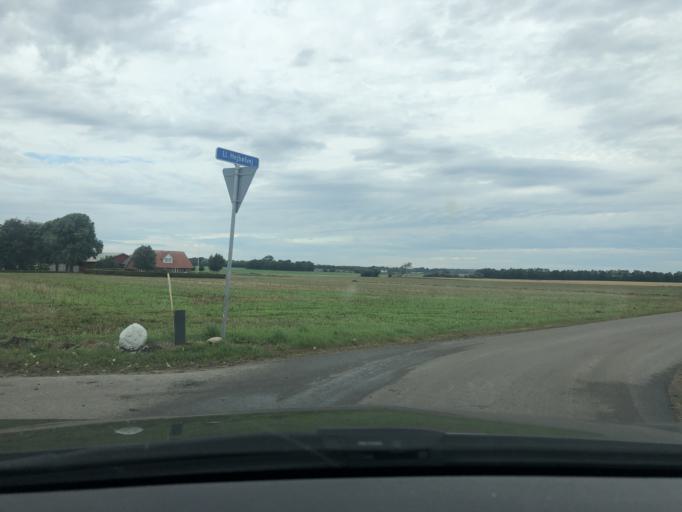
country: DK
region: South Denmark
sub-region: Varde Kommune
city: Olgod
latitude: 55.7971
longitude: 8.6904
